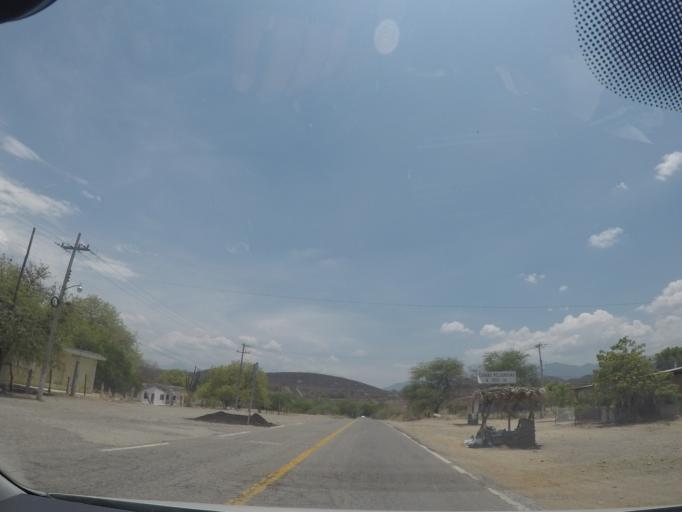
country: MX
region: Oaxaca
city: Magdalena Tequisistlan
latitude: 16.4141
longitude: -95.6053
